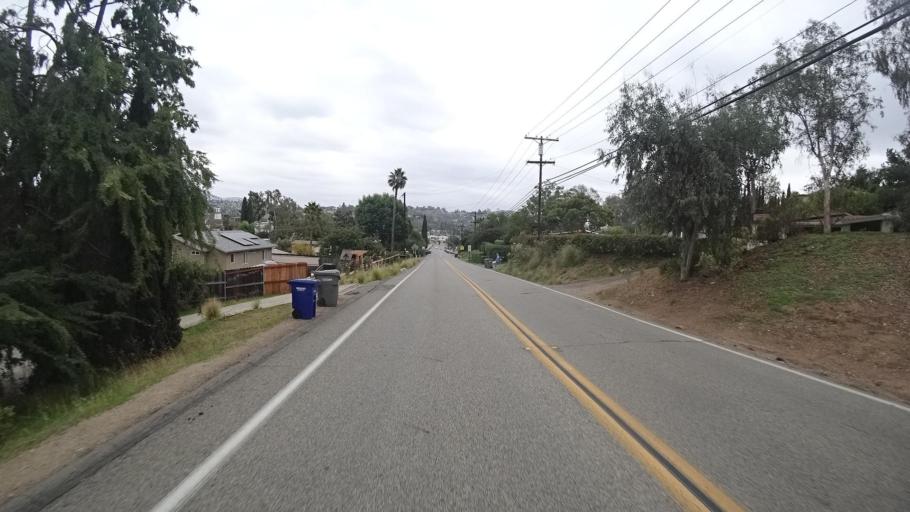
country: US
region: California
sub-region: San Diego County
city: Spring Valley
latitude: 32.7523
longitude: -116.9873
